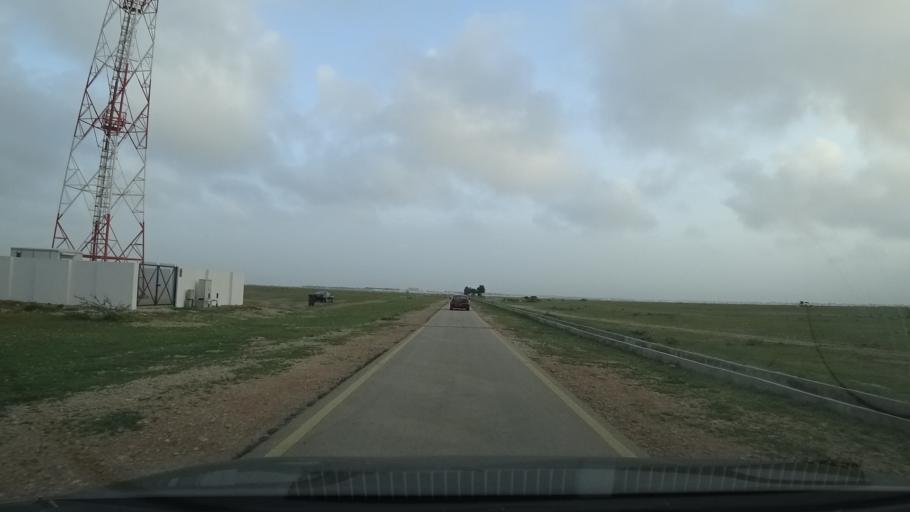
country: OM
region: Zufar
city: Salalah
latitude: 17.0869
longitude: 54.2324
